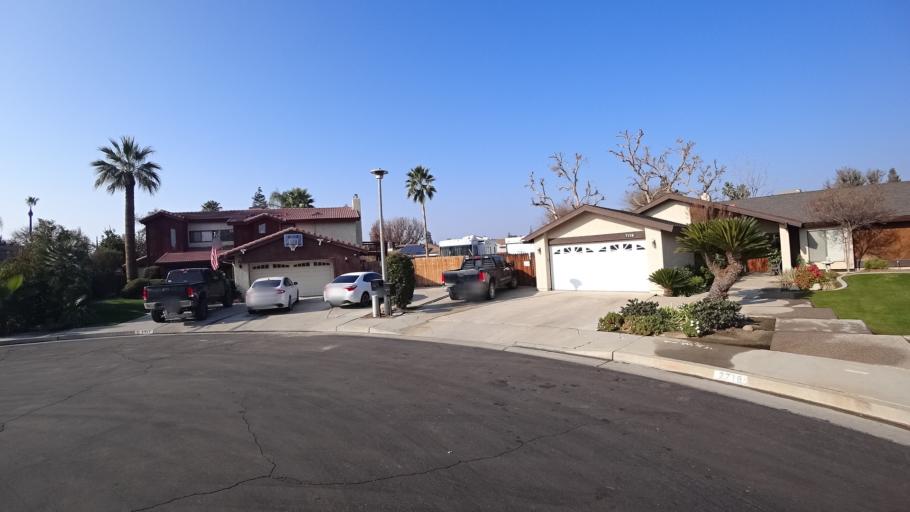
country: US
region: California
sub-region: Kern County
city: Greenacres
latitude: 35.3355
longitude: -119.0884
